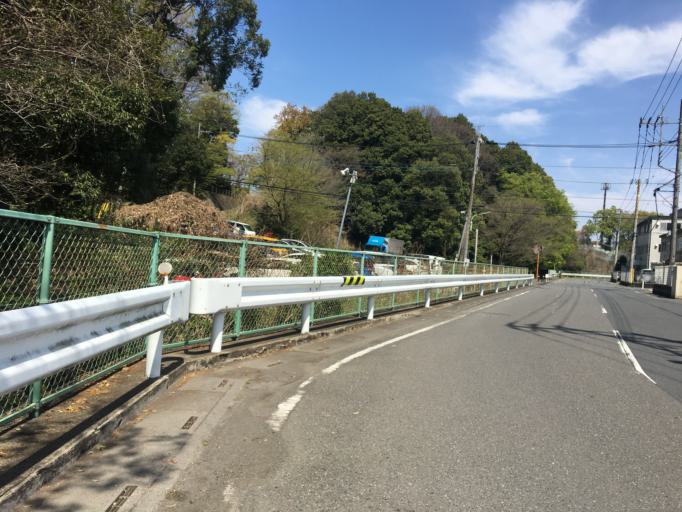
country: JP
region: Saitama
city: Shiki
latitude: 35.8217
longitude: 139.5489
